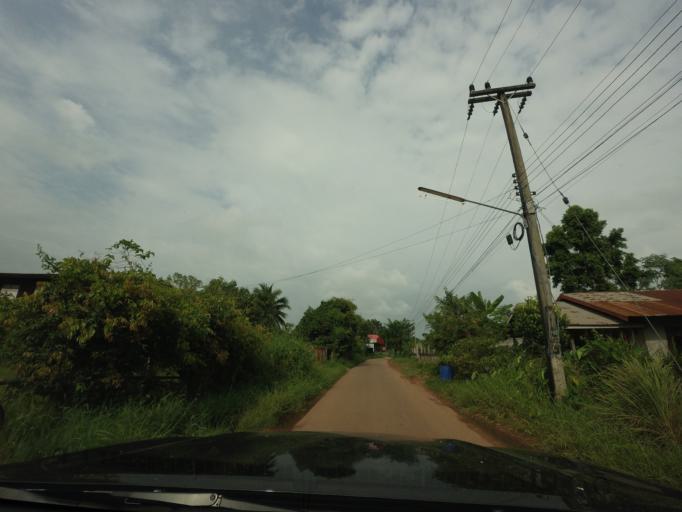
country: TH
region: Nong Khai
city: Nong Khai
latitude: 17.8151
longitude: 102.7209
